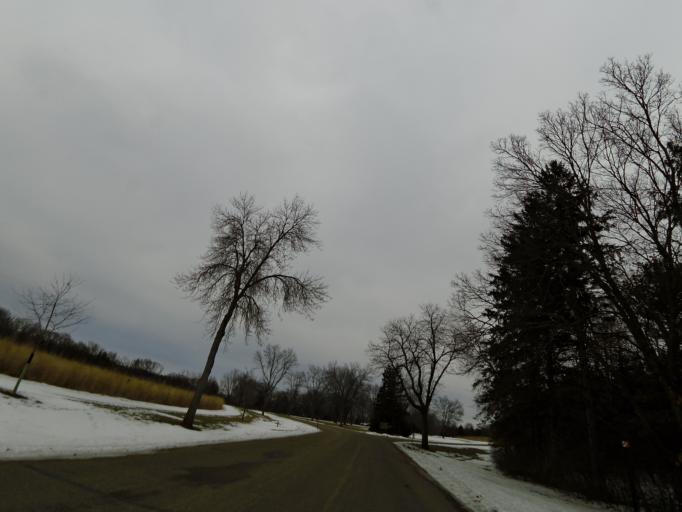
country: US
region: Wisconsin
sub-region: Pierce County
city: Prescott
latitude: 44.8022
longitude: -92.7991
